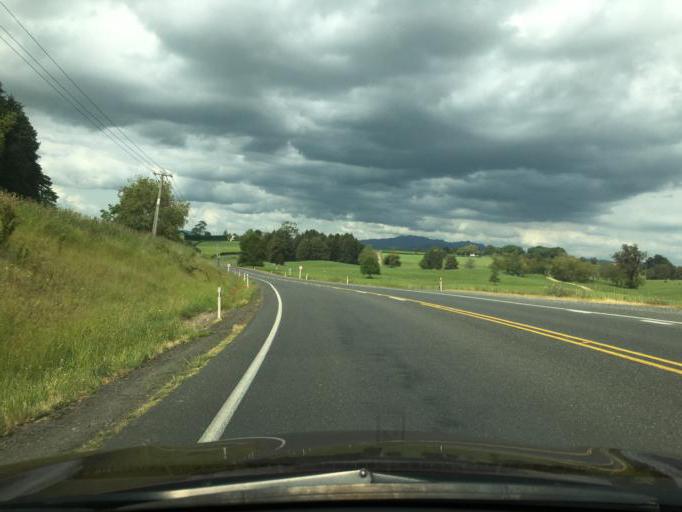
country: NZ
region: Waikato
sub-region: Waipa District
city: Cambridge
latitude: -38.0155
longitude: 175.3621
